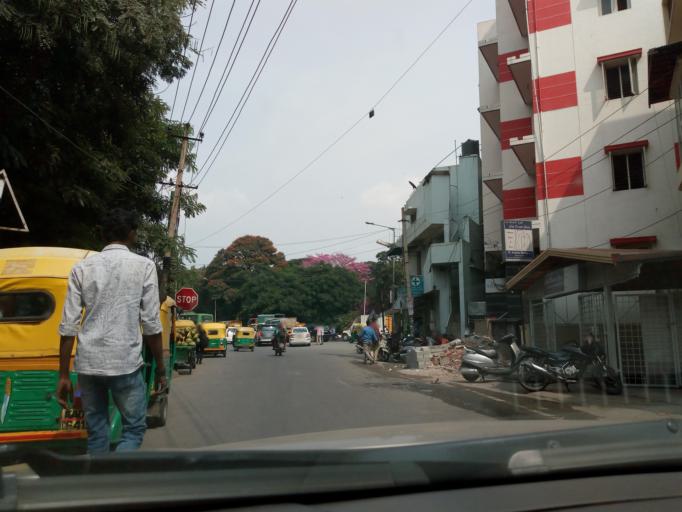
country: IN
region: Karnataka
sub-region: Bangalore Urban
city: Bangalore
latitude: 12.9273
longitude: 77.6159
